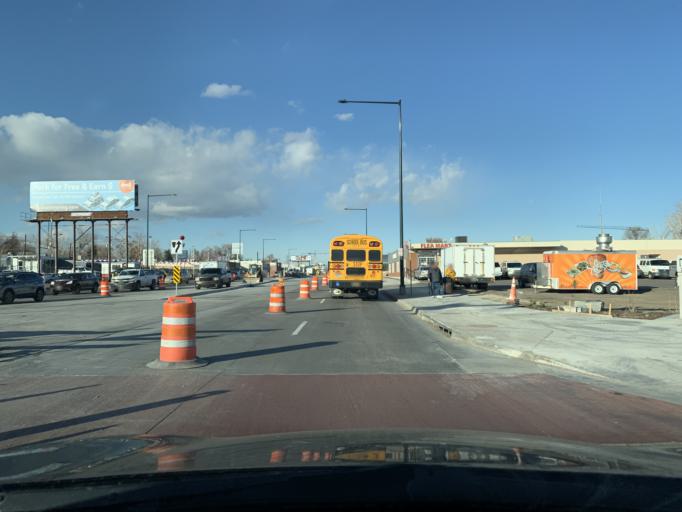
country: US
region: Colorado
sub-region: Denver County
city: Denver
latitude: 39.7294
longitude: -105.0249
